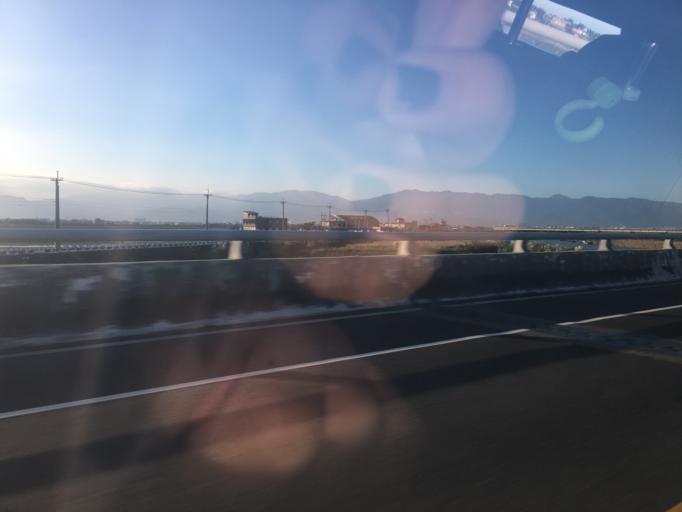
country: TW
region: Taiwan
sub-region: Yilan
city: Yilan
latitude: 24.7173
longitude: 121.8206
